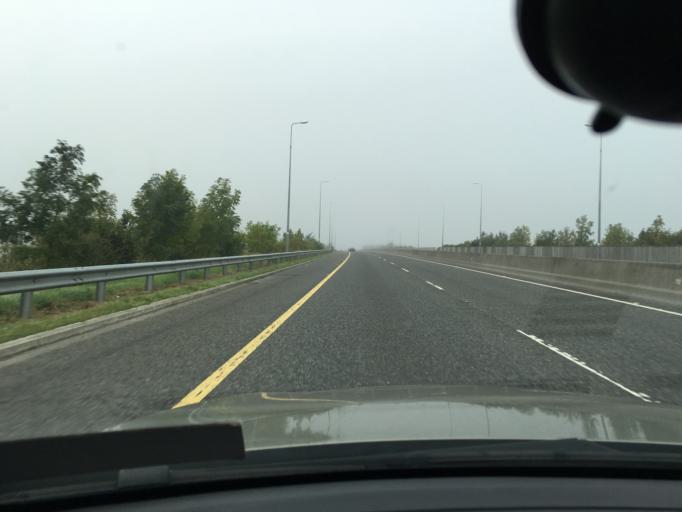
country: IE
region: Leinster
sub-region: An Iarmhi
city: Moate
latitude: 53.3927
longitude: -7.7799
